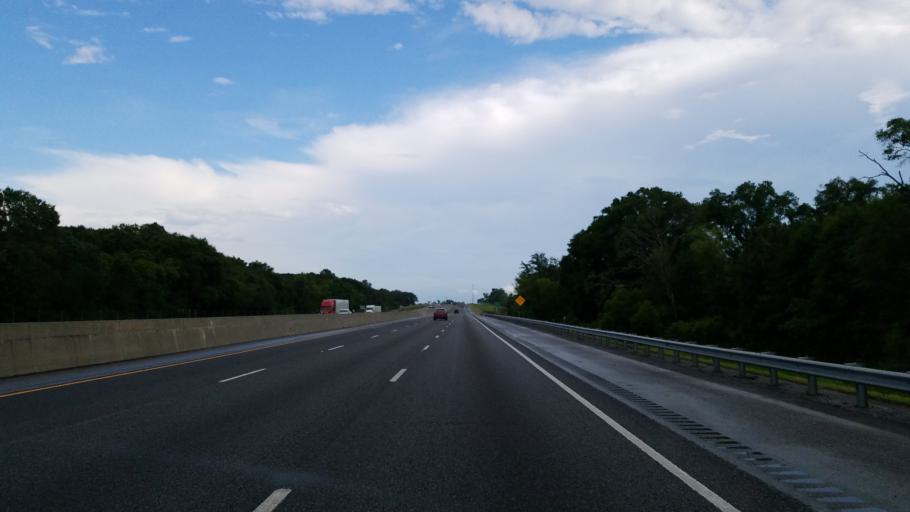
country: US
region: Georgia
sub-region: Turner County
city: Ashburn
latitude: 31.5998
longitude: -83.5616
